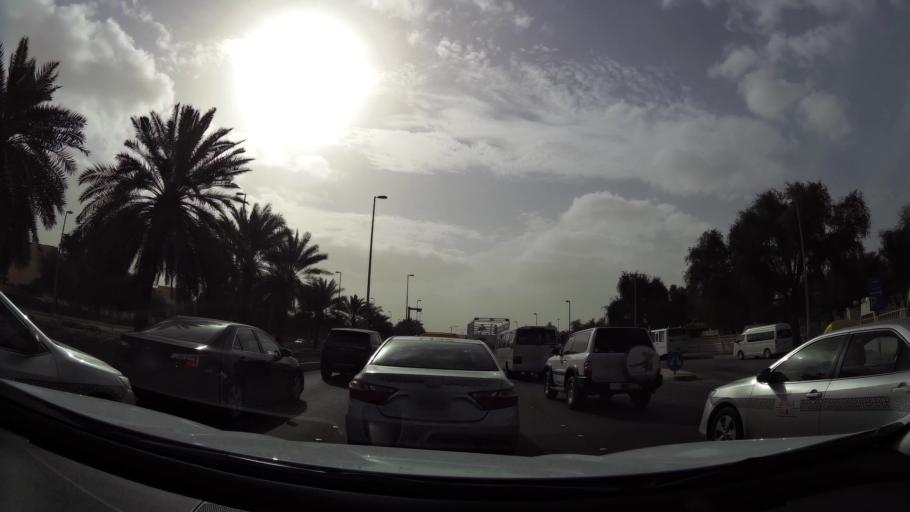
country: AE
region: Abu Dhabi
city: Abu Dhabi
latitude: 24.4302
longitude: 54.4420
